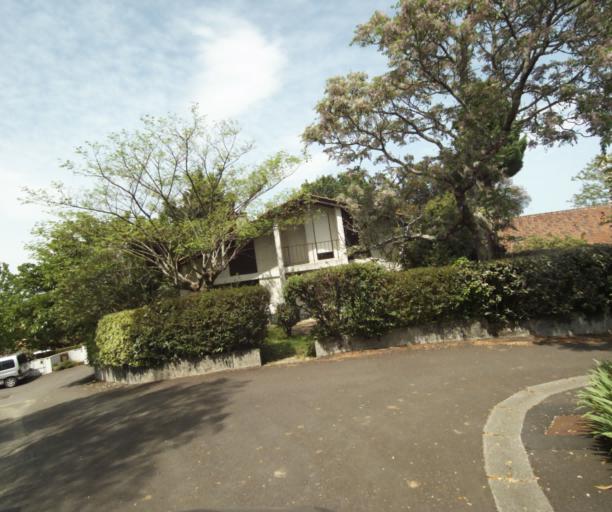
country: FR
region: Aquitaine
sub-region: Departement des Pyrenees-Atlantiques
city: Mouguerre
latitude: 43.4590
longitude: -1.4401
